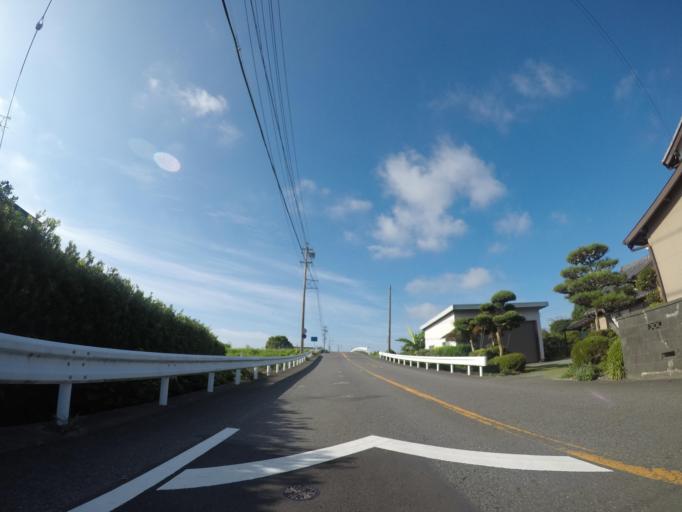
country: JP
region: Shizuoka
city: Yaizu
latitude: 34.8212
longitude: 138.3114
